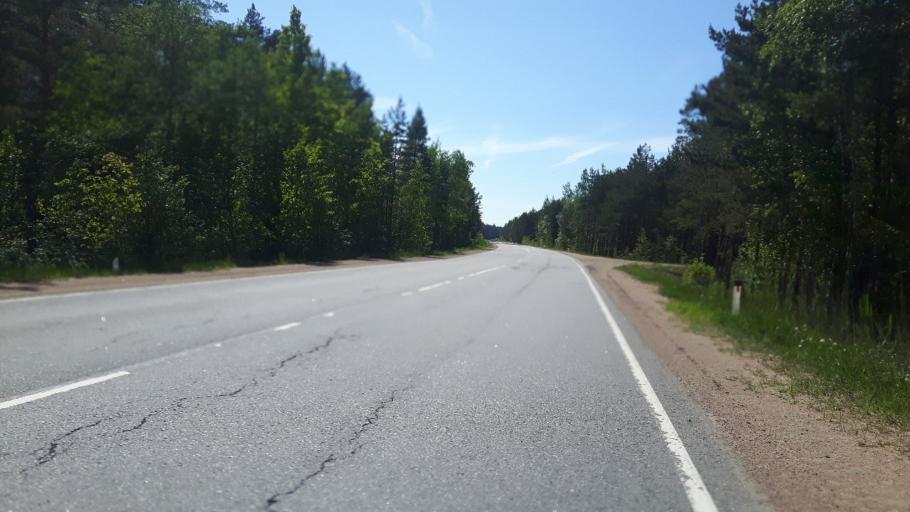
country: RU
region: Leningrad
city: Sista-Palkino
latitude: 59.7691
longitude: 28.7665
